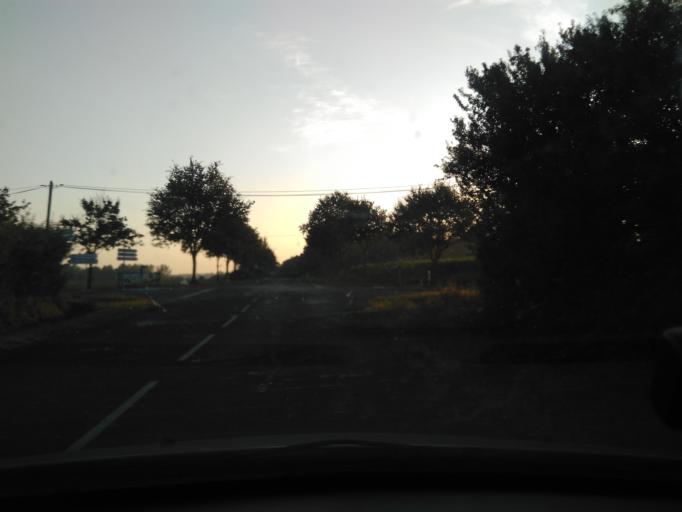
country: FR
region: Pays de la Loire
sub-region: Departement de la Vendee
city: Les Brouzils
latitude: 46.8825
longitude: -1.3135
